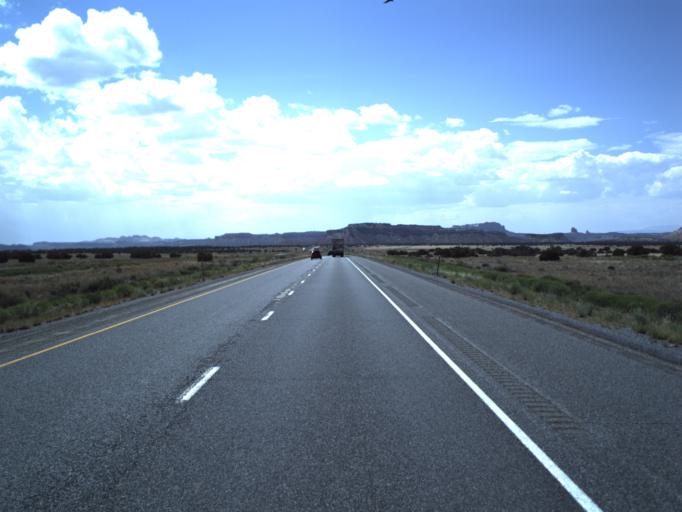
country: US
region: Utah
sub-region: Emery County
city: Castle Dale
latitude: 38.8957
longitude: -110.6103
